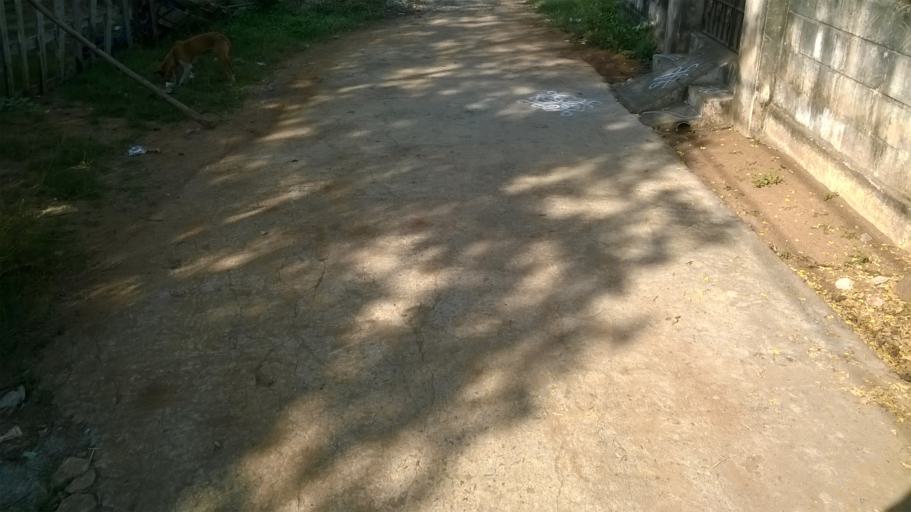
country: IN
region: Tamil Nadu
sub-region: Kancheepuram
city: Vandalur
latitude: 12.8848
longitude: 80.0820
